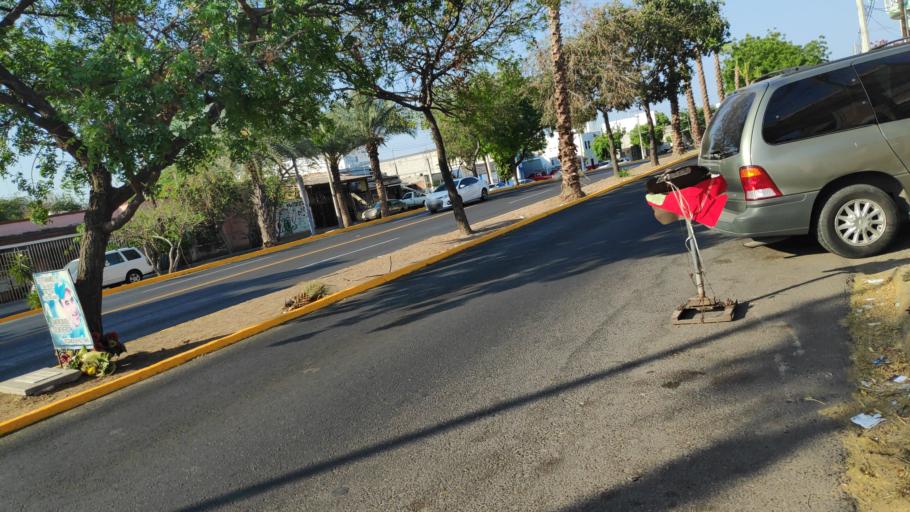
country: MX
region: Sinaloa
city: Culiacan
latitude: 24.7939
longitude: -107.4087
